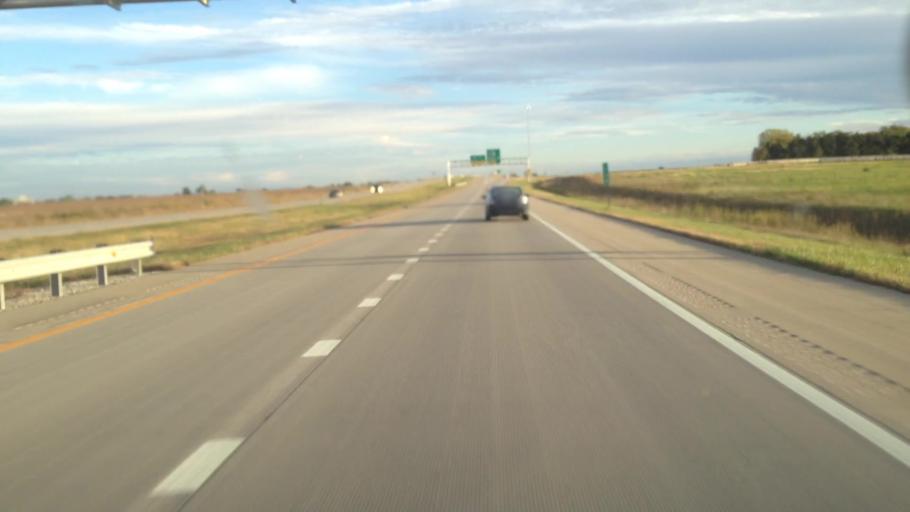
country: US
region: Kansas
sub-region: Franklin County
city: Ottawa
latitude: 38.6442
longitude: -95.2267
